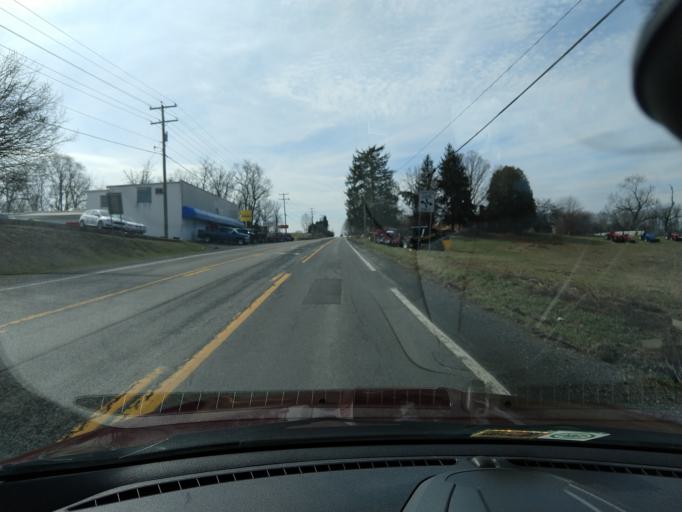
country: US
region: West Virginia
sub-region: Greenbrier County
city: Lewisburg
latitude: 37.8556
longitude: -80.4124
